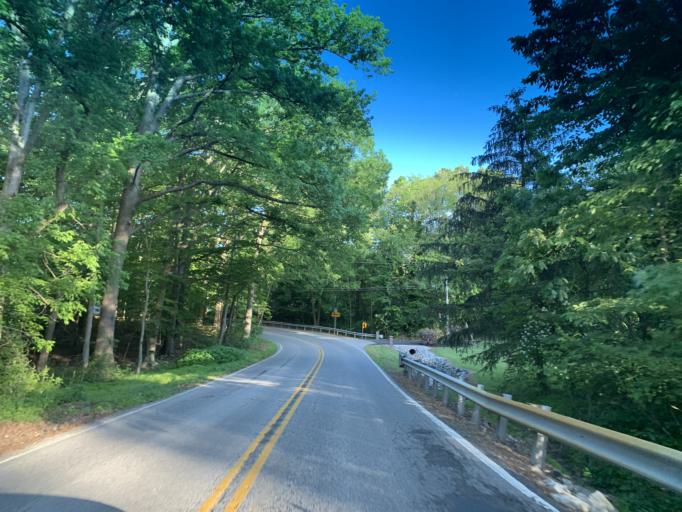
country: US
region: Maryland
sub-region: Cecil County
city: Elkton
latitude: 39.6633
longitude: -75.8366
